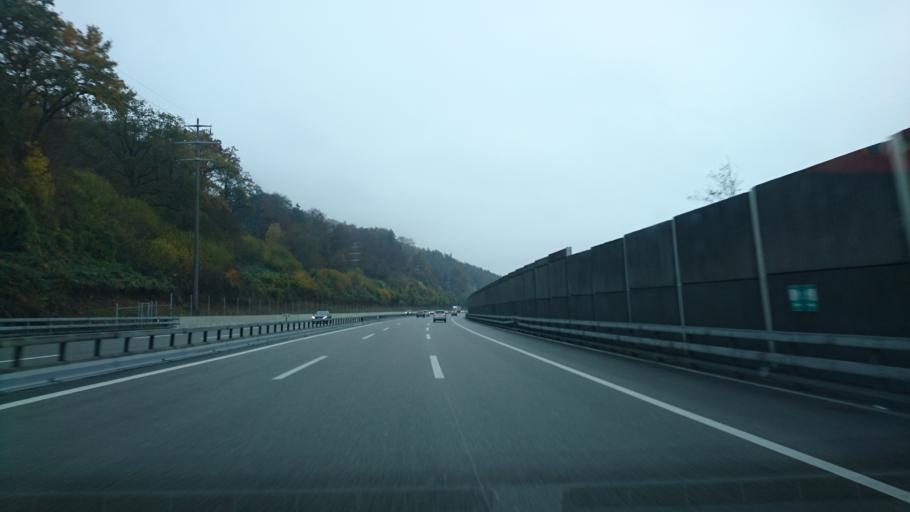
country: CH
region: Solothurn
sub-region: Bezirk Olten
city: Gunzgen
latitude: 47.3118
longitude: 7.8524
